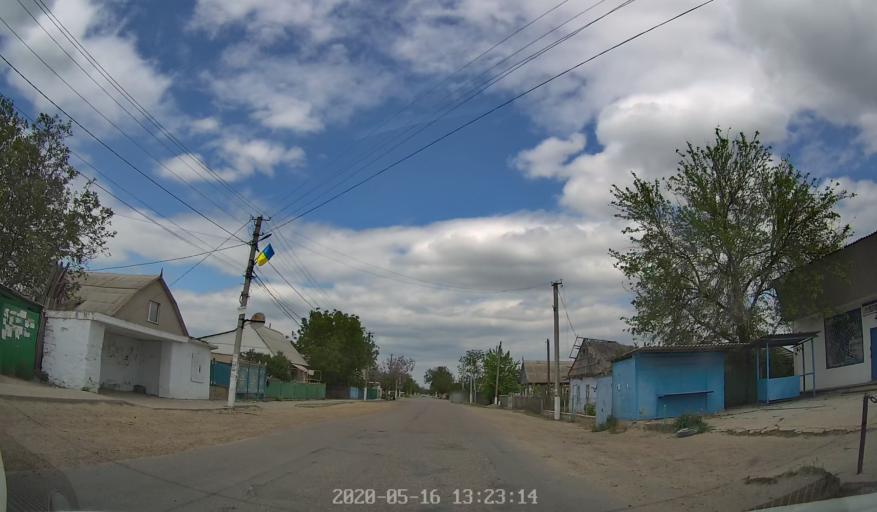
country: MD
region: Telenesti
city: Dnestrovsc
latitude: 46.5363
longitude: 30.0153
